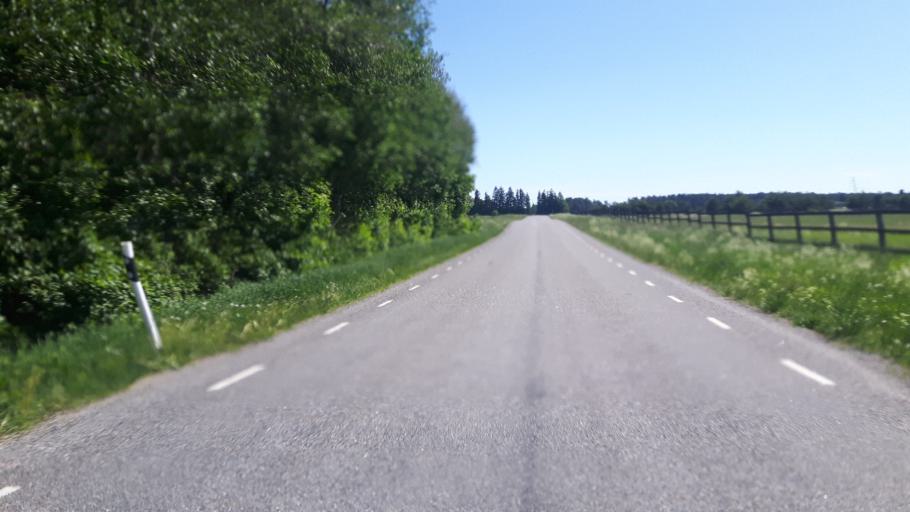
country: EE
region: Raplamaa
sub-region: Kohila vald
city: Kohila
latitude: 59.1993
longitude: 24.6940
